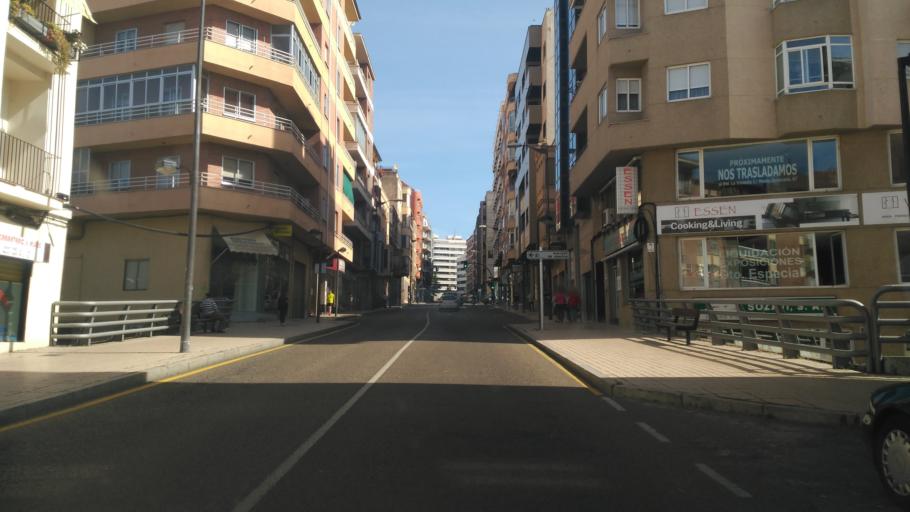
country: ES
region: Castille and Leon
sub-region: Provincia de Zamora
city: Zamora
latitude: 41.5033
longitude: -5.7399
